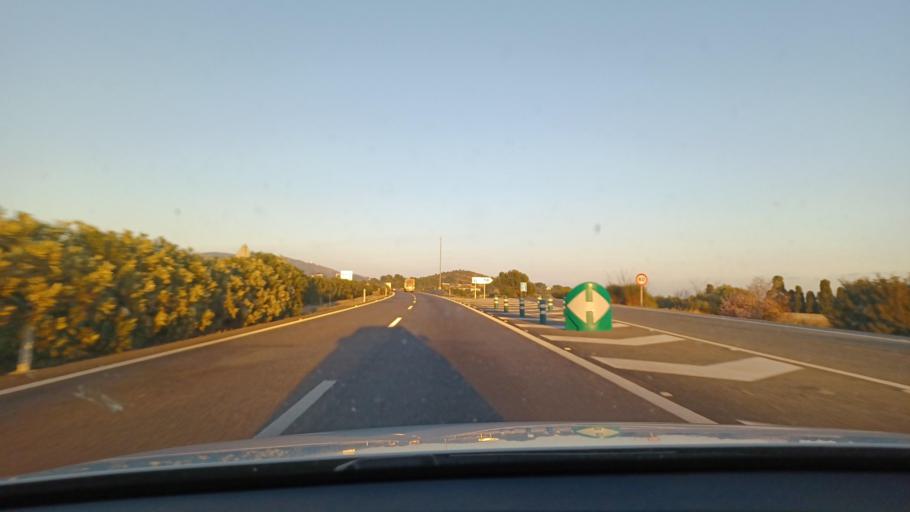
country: ES
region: Valencia
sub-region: Provincia de Castello
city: Torreblanca
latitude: 40.2269
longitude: 0.2022
